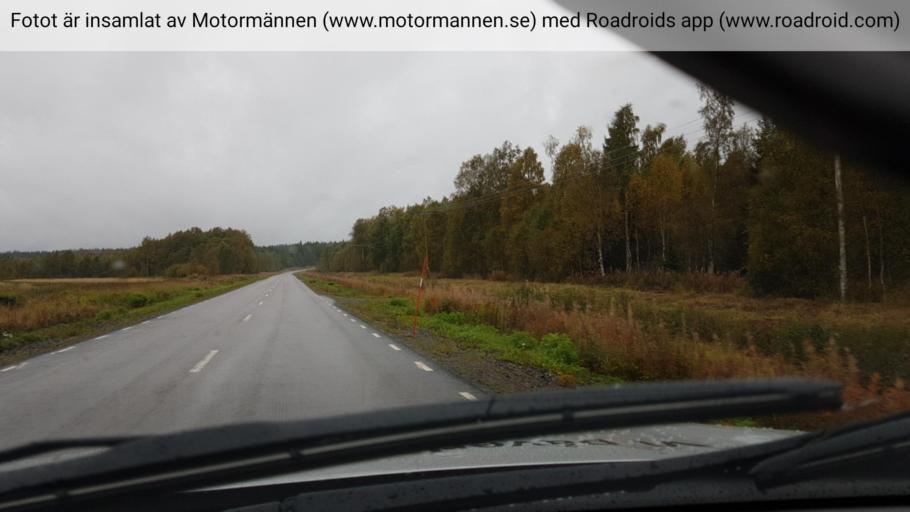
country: SE
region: Norrbotten
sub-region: Lulea Kommun
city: Sodra Sunderbyn
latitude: 65.8234
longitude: 21.9253
